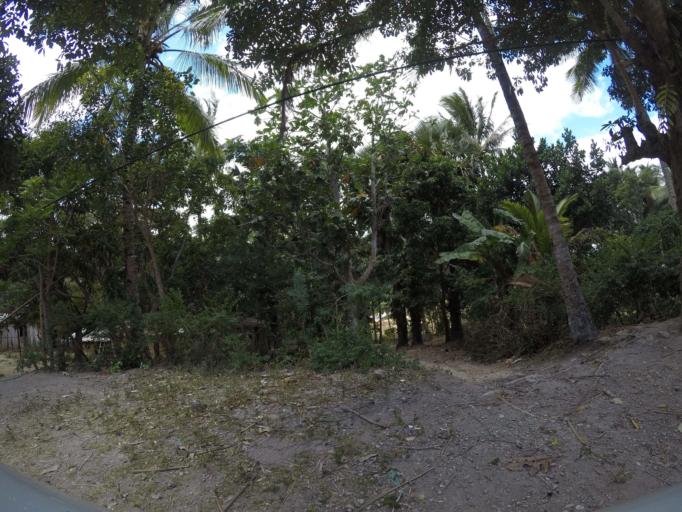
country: TL
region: Lautem
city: Lospalos
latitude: -8.5375
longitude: 126.8280
